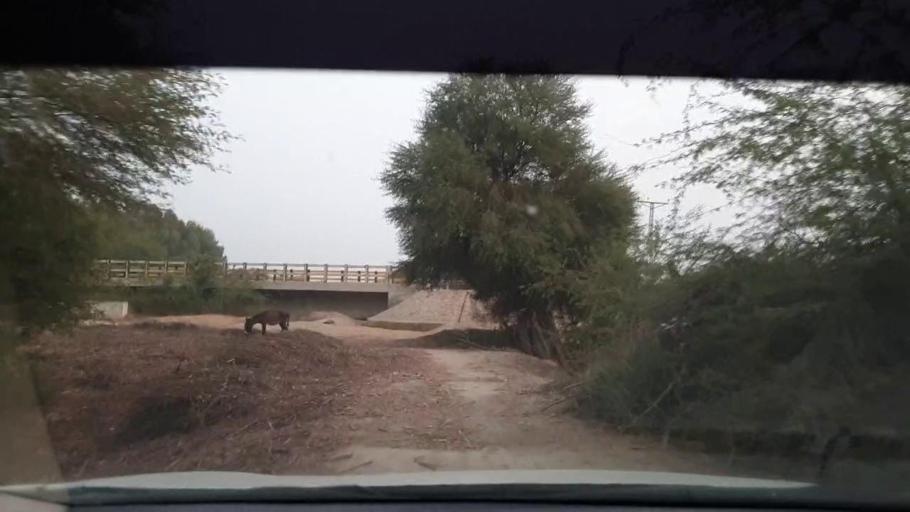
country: PK
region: Sindh
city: Berani
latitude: 25.8441
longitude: 68.7890
